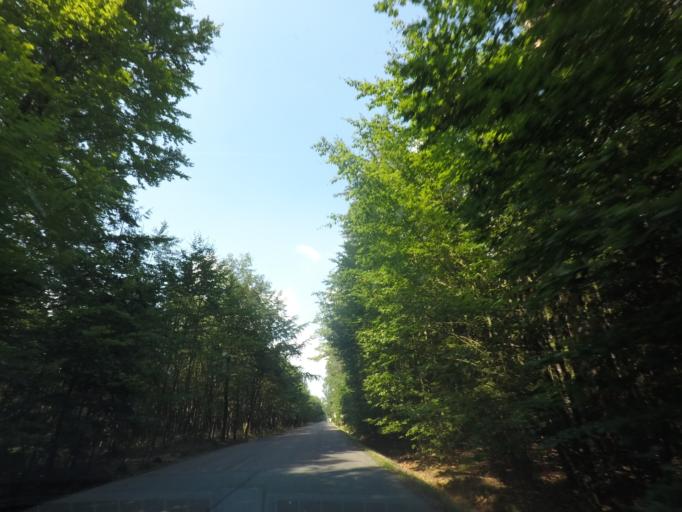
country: CZ
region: Pardubicky
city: Horni Jeleni
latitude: 50.0620
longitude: 16.0823
